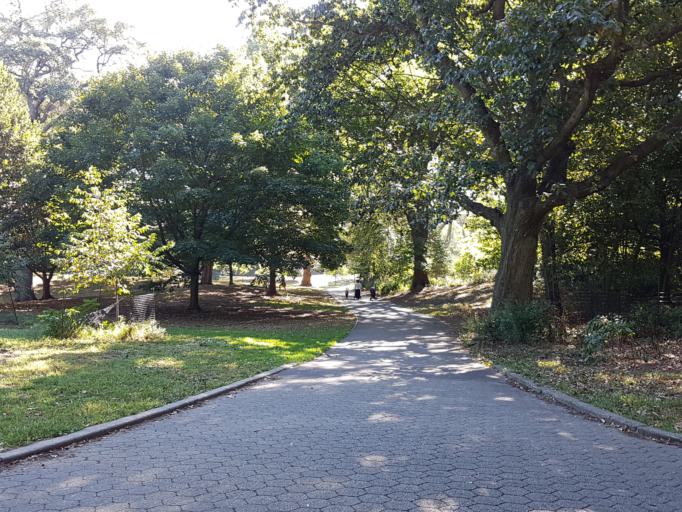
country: US
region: New York
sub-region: Kings County
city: Brooklyn
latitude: 40.6673
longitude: -73.9717
